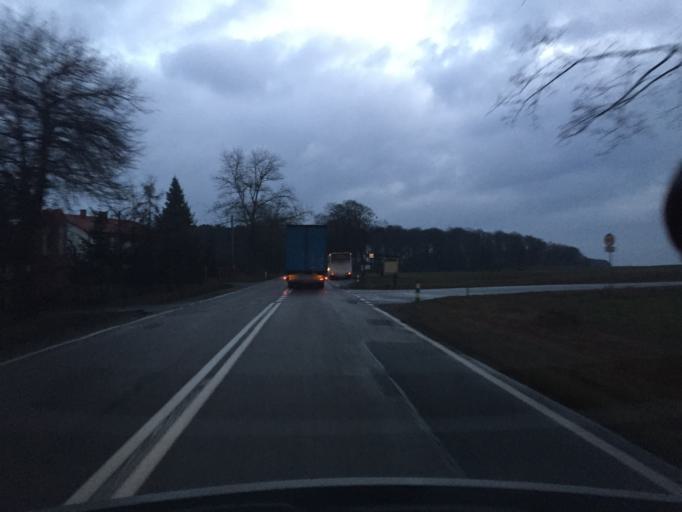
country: PL
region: Kujawsko-Pomorskie
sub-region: Powiat brodnicki
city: Bobrowo
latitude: 53.2288
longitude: 19.2223
